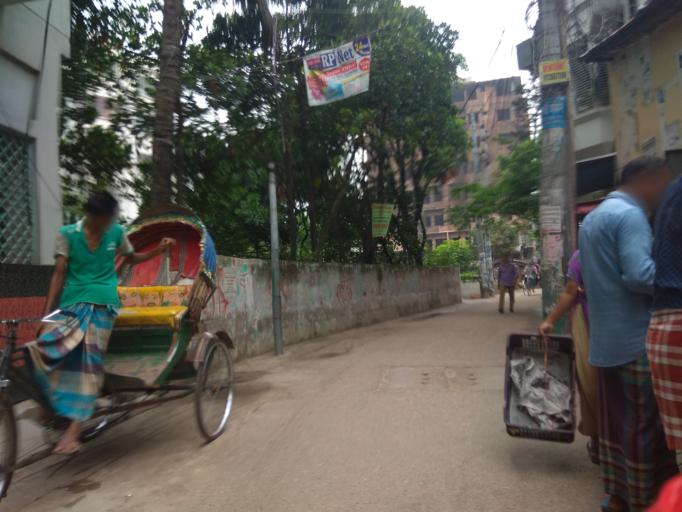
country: BD
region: Dhaka
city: Azimpur
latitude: 23.7941
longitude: 90.3686
